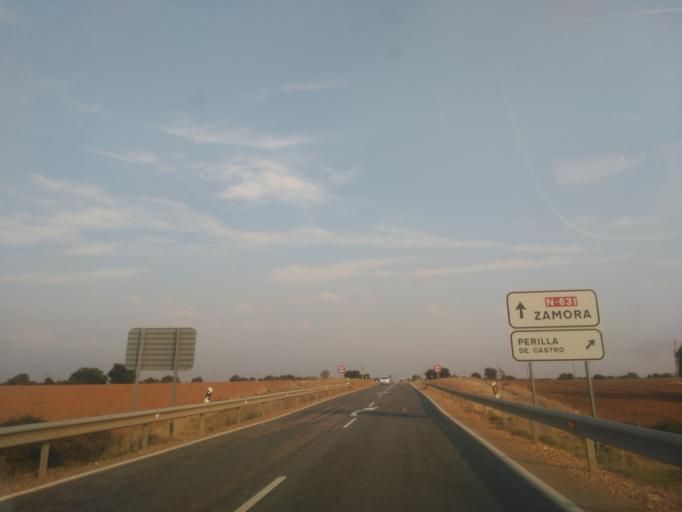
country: ES
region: Castille and Leon
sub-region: Provincia de Zamora
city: Perilla de Castro
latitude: 41.7372
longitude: -5.8297
